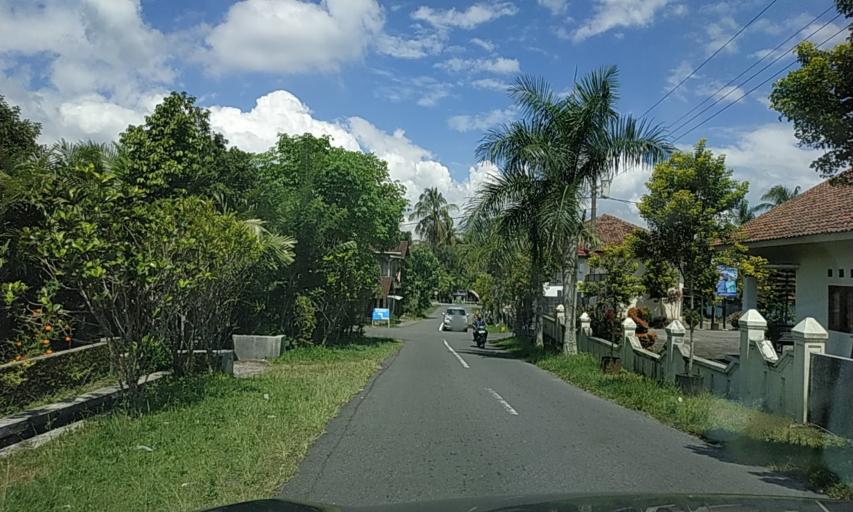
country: ID
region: Central Java
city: Muntilan
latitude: -7.6206
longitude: 110.3830
